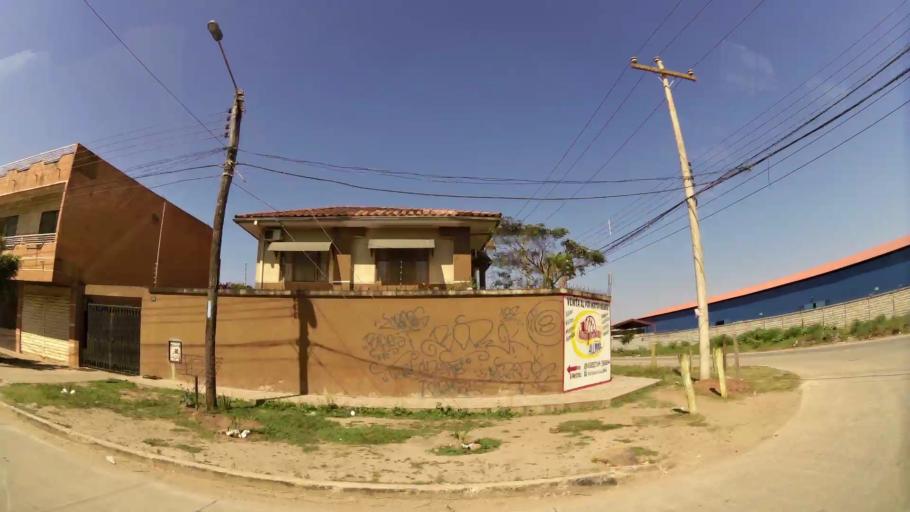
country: BO
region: Santa Cruz
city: Santa Cruz de la Sierra
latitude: -17.7536
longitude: -63.1504
